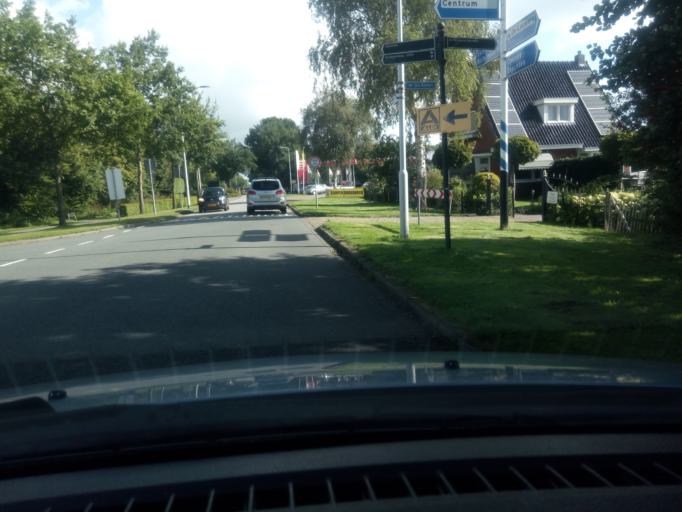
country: NL
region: Friesland
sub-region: Gemeente Achtkarspelen
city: Surhuisterveen
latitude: 53.1843
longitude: 6.1822
